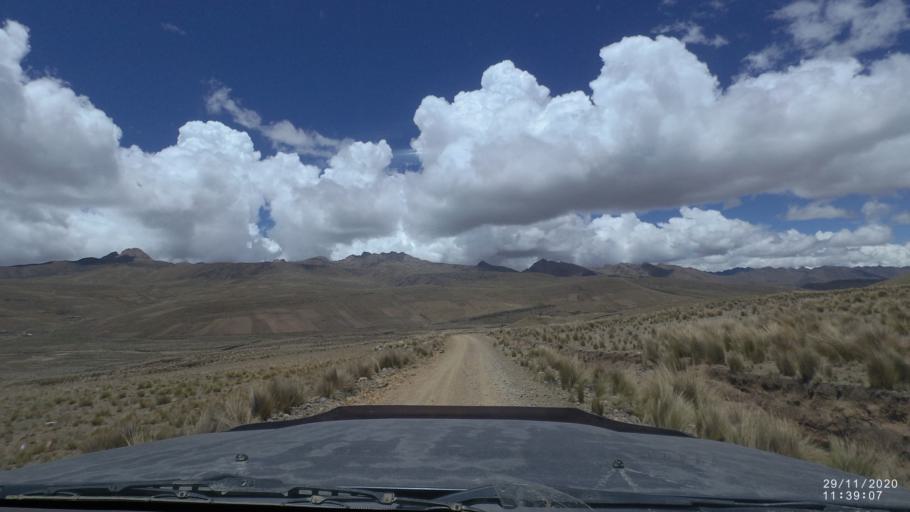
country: BO
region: Cochabamba
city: Cochabamba
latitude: -17.1977
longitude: -66.2380
